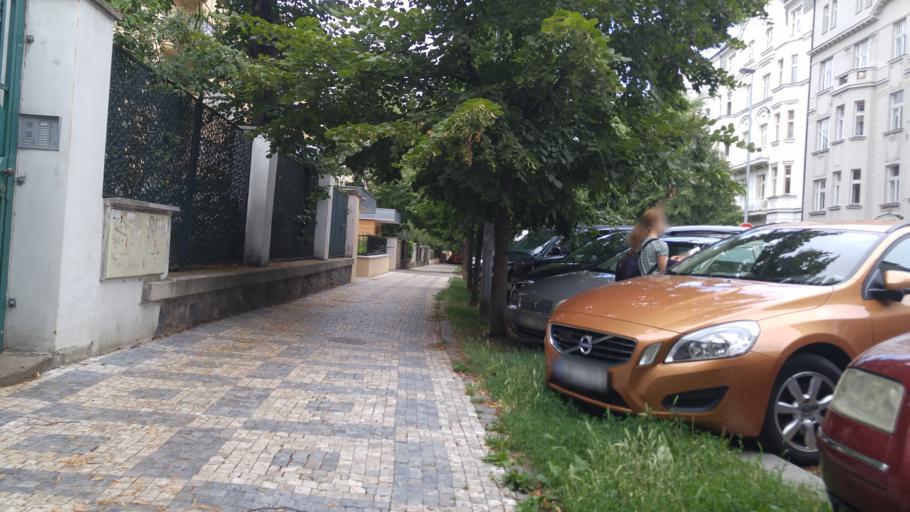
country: CZ
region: Praha
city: Prague
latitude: 50.1014
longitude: 14.4234
